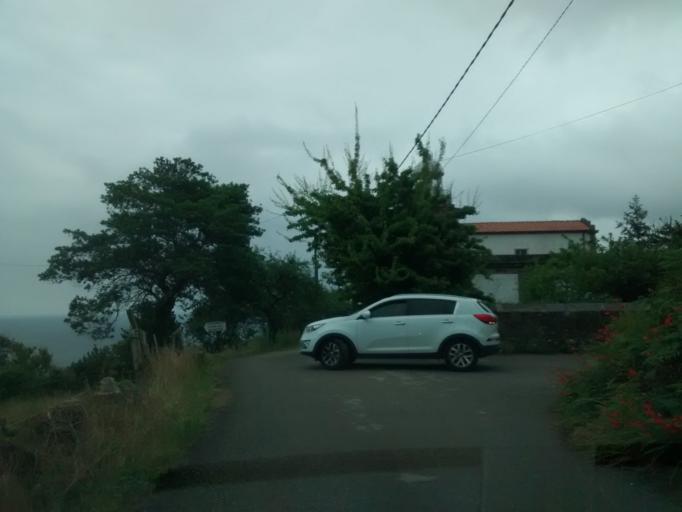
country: ES
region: Asturias
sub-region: Province of Asturias
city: Villaviciosa
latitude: 43.5479
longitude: -5.3997
